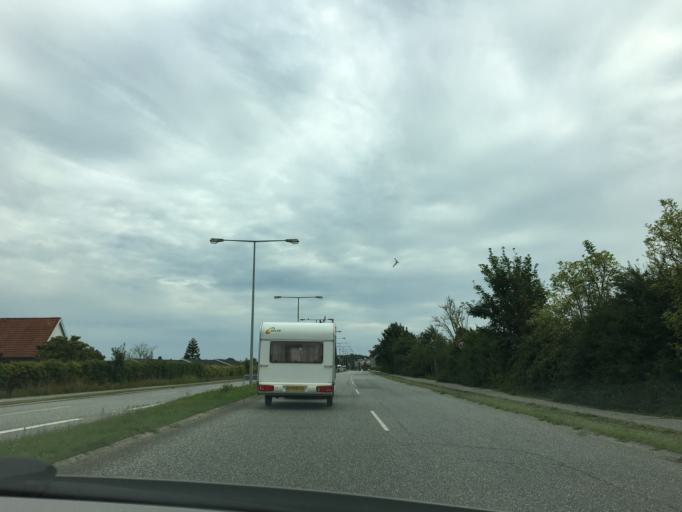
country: DK
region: South Denmark
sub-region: Fredericia Kommune
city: Fredericia
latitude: 55.5668
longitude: 9.7245
